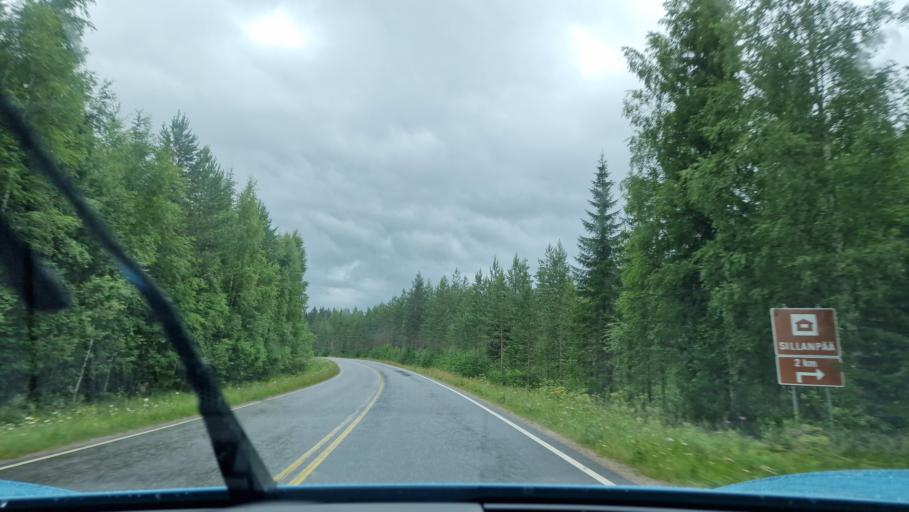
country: FI
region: Southern Ostrobothnia
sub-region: Jaerviseutu
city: Soini
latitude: 62.7845
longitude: 24.3877
